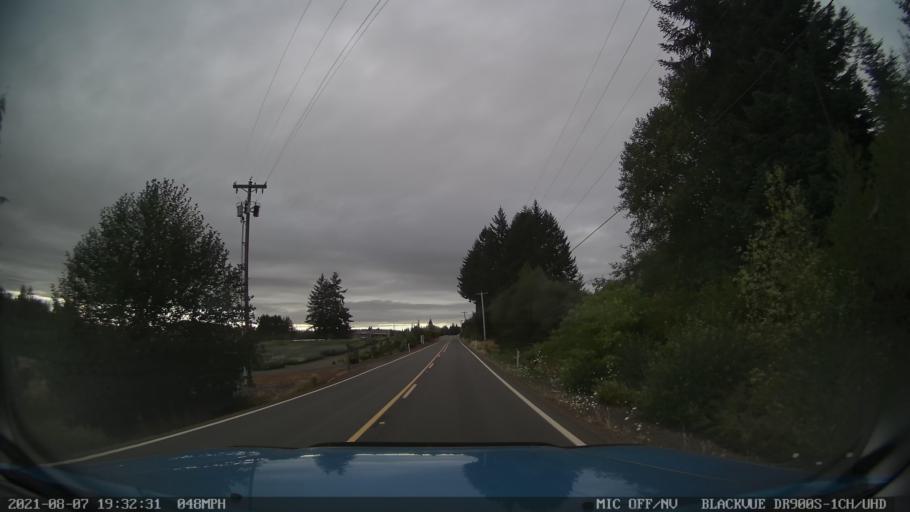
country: US
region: Oregon
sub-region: Linn County
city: Lyons
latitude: 44.9006
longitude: -122.6447
